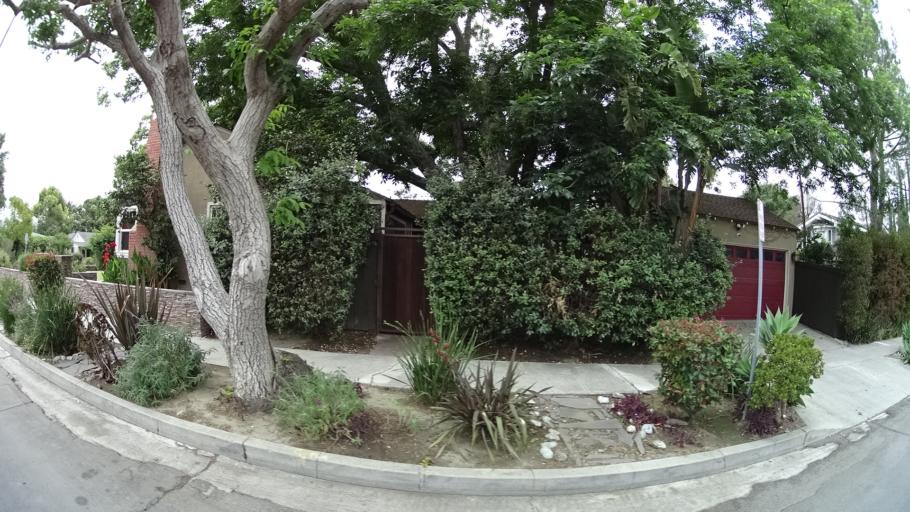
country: US
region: California
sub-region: Los Angeles County
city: Universal City
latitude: 34.1621
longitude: -118.3535
